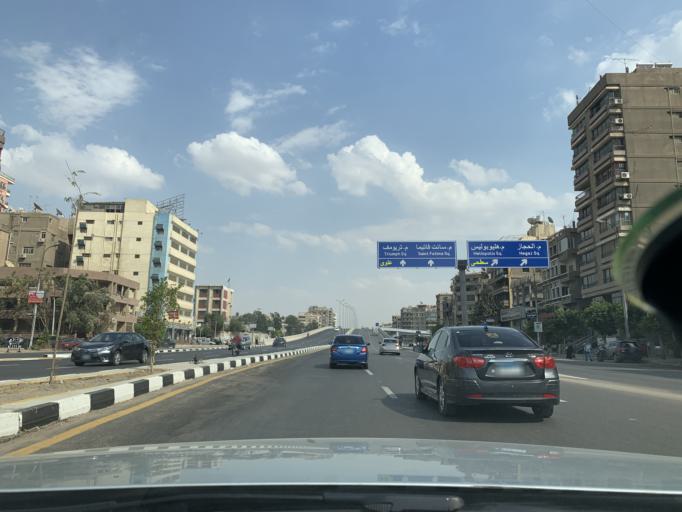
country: EG
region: Muhafazat al Qalyubiyah
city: Al Khankah
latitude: 30.1138
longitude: 31.3440
